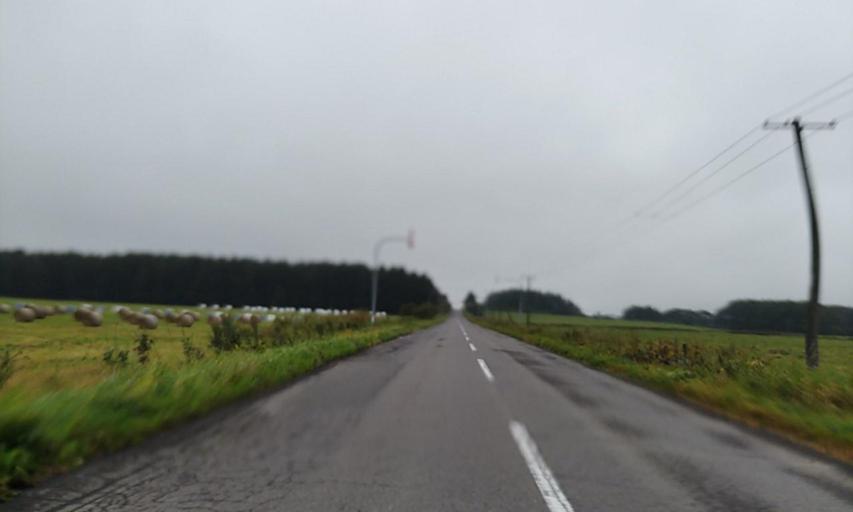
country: JP
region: Hokkaido
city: Shibetsu
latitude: 43.5092
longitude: 144.6684
